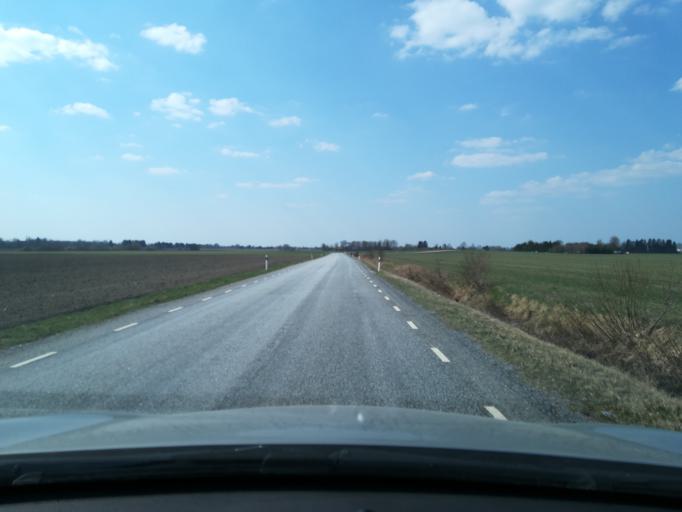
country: EE
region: Harju
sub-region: Saue linn
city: Saue
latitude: 59.3368
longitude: 24.5733
